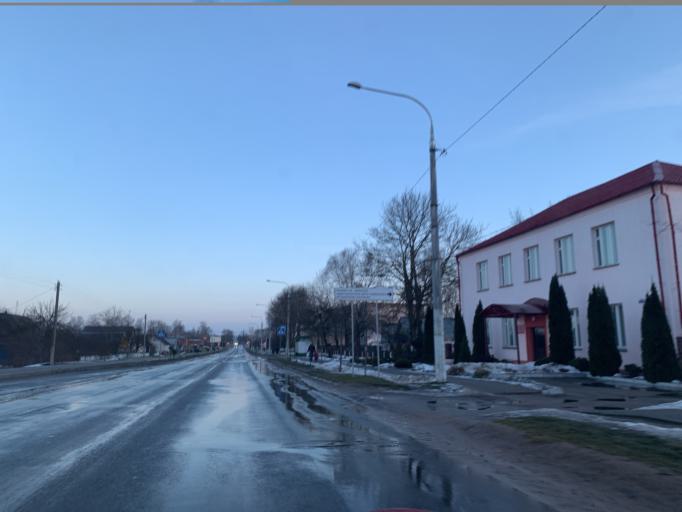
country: BY
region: Minsk
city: Nyasvizh
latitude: 53.2287
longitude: 26.6620
